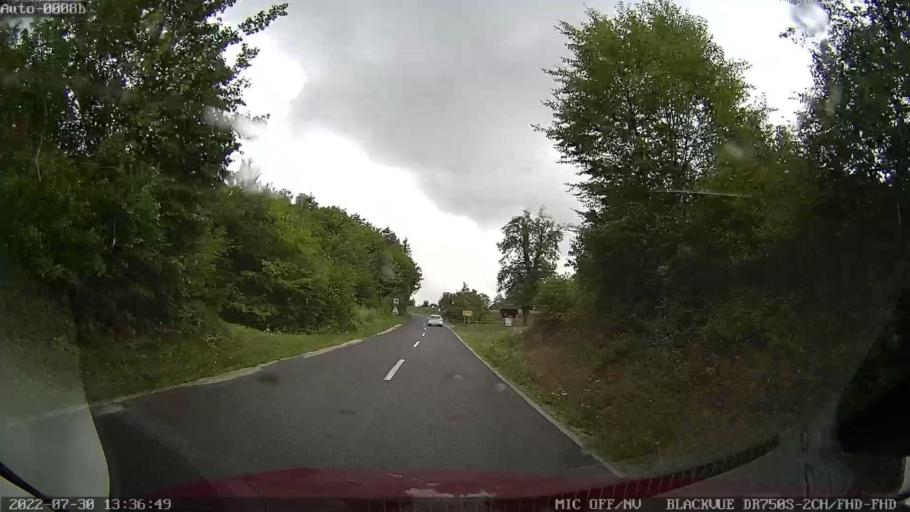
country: SI
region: Zuzemberk
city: Zuzemberk
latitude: 45.8727
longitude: 14.9217
